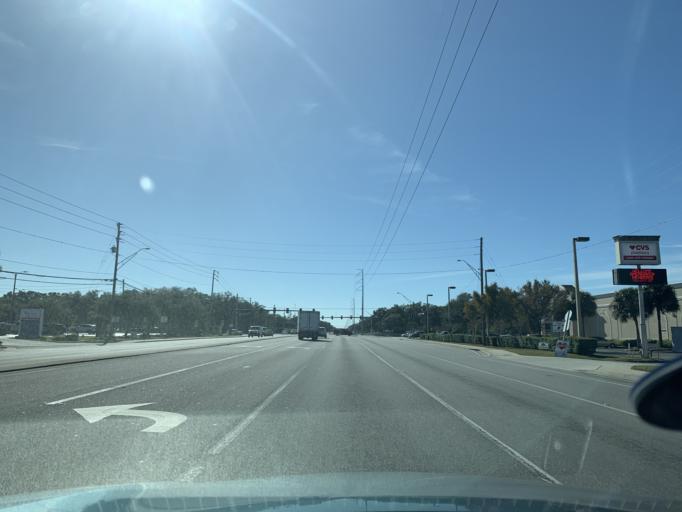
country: US
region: Florida
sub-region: Pinellas County
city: Largo
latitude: 27.8739
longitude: -82.7624
